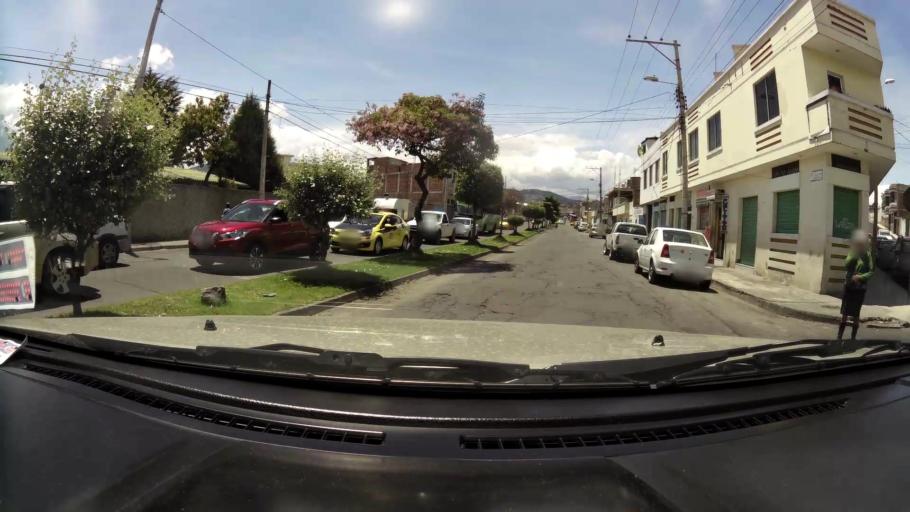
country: EC
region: Chimborazo
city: Riobamba
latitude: -1.6785
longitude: -78.6390
